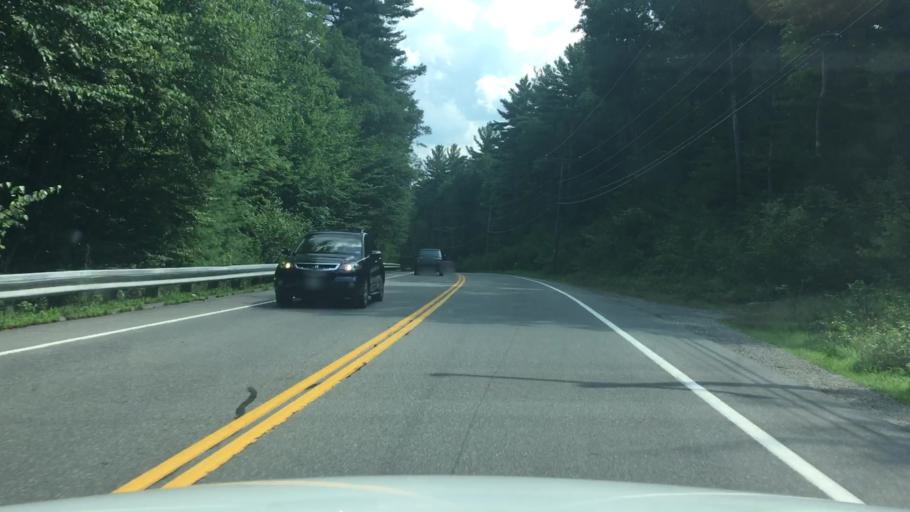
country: US
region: New Hampshire
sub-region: Rockingham County
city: Auburn
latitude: 42.9920
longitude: -71.3792
